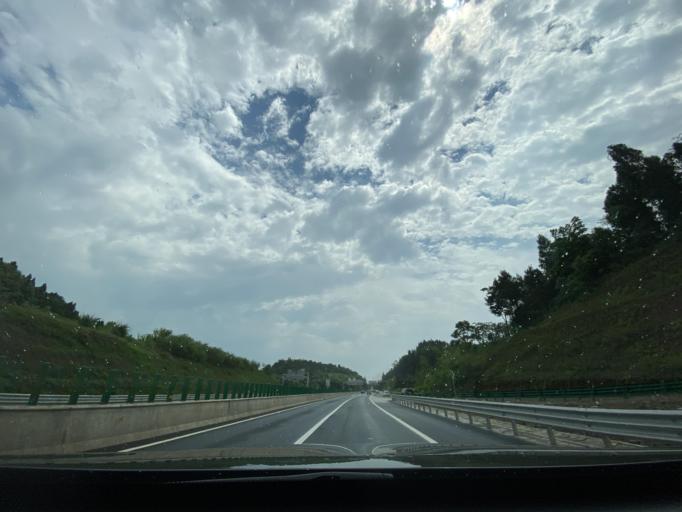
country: CN
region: Sichuan
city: Yanjiang
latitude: 30.2049
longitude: 104.5989
